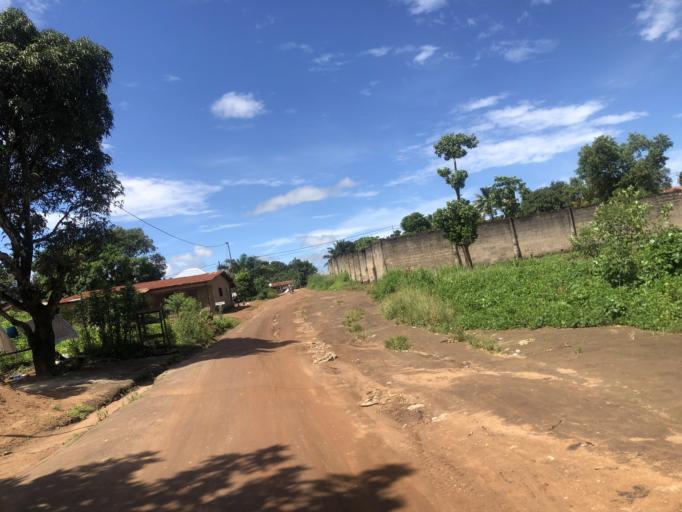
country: SL
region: Eastern Province
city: Koidu
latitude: 8.6380
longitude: -10.9539
